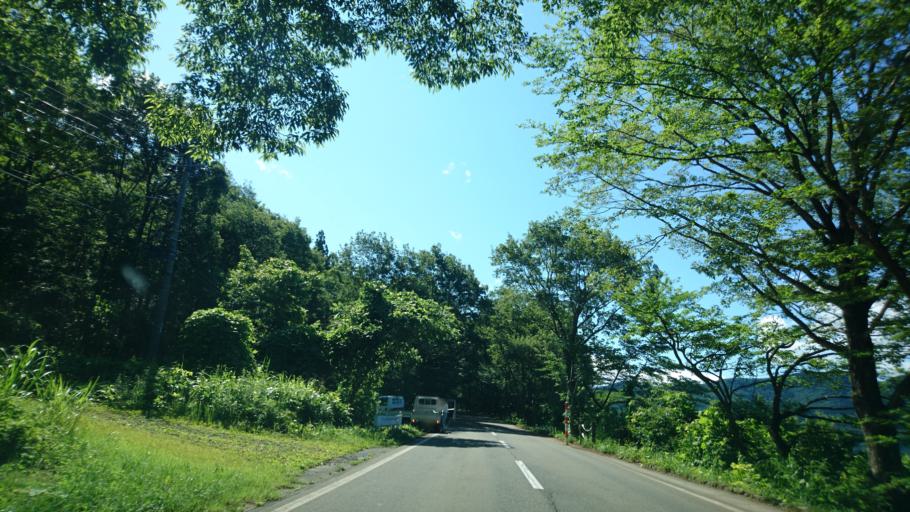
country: JP
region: Akita
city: Kakunodatemachi
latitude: 39.7420
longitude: 140.6875
